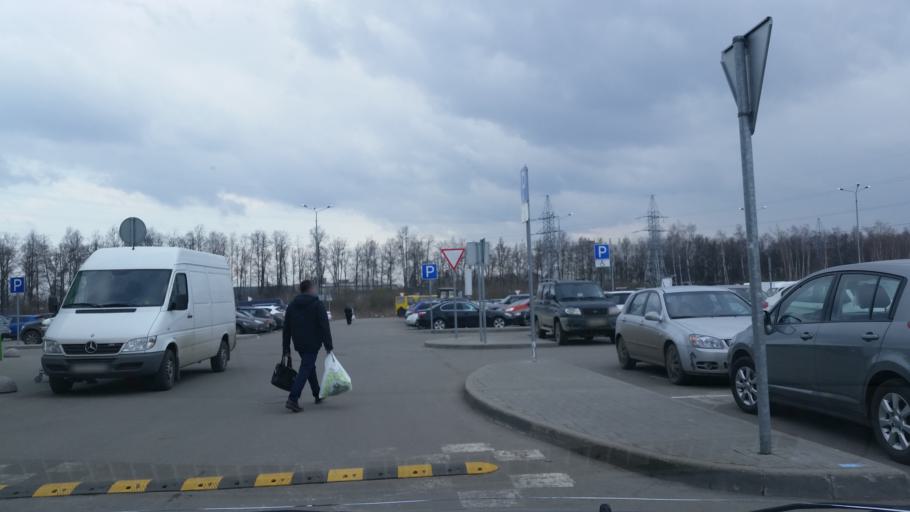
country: RU
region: Moskovskaya
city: Arkhangel'skoye
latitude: 55.7993
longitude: 37.2990
